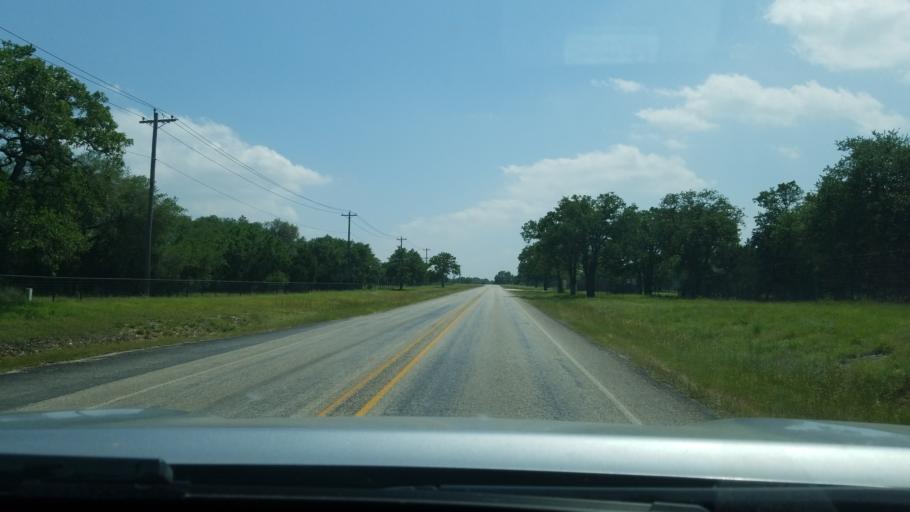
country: US
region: Texas
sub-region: Bexar County
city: Fair Oaks Ranch
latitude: 29.8824
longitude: -98.5573
